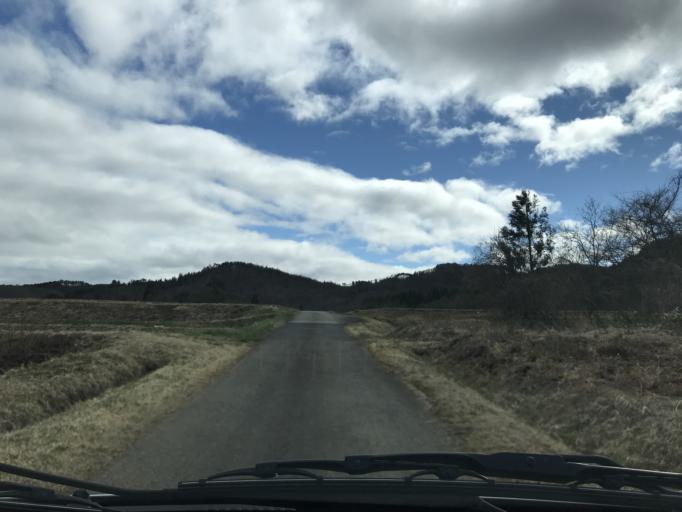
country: JP
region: Iwate
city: Mizusawa
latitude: 39.0784
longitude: 140.9890
